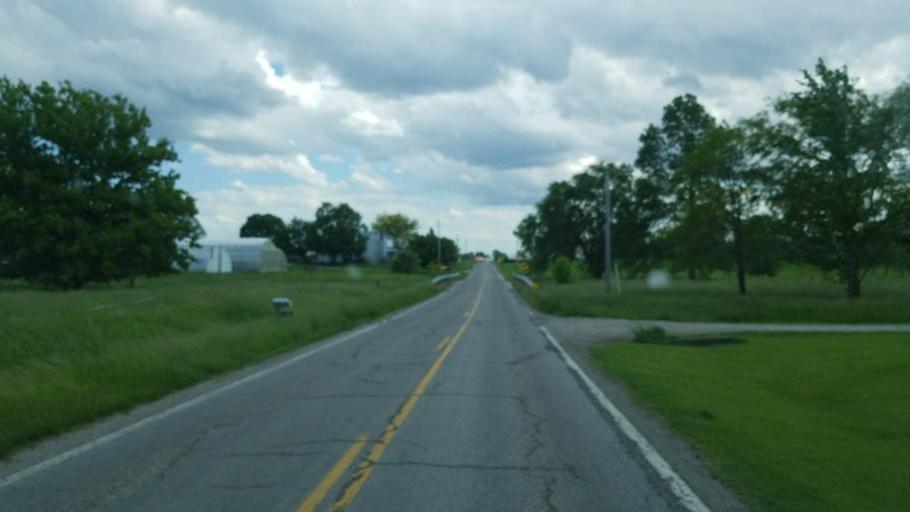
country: US
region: Ohio
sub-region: Huron County
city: Plymouth
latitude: 41.0023
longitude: -82.6065
